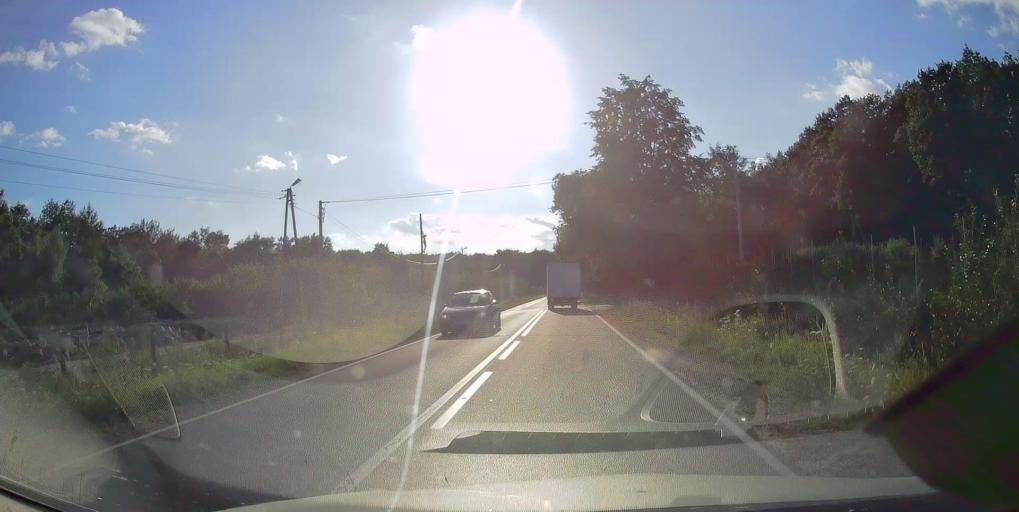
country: PL
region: Masovian Voivodeship
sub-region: Powiat grojecki
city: Bledow
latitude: 51.8037
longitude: 20.5955
